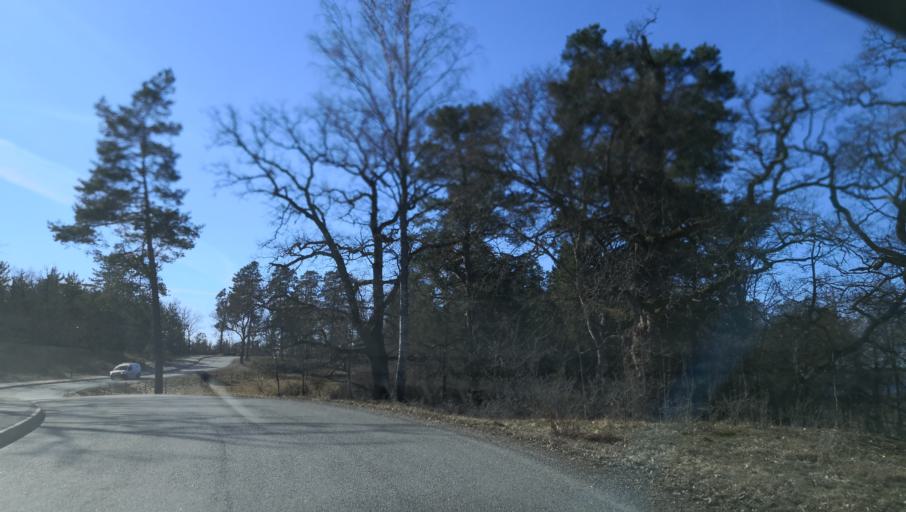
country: SE
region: Stockholm
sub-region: Varmdo Kommun
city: Gustavsberg
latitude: 59.3108
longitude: 18.3581
